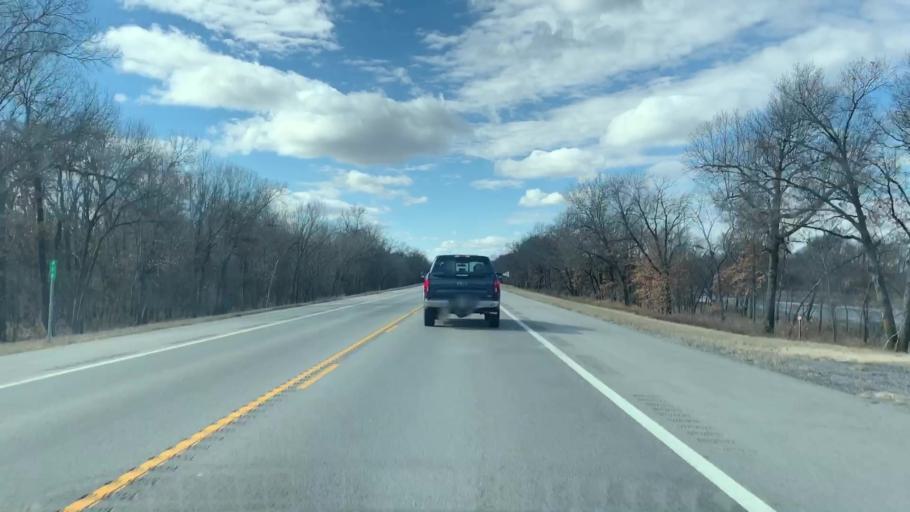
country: US
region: Kansas
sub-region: Cherokee County
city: Columbus
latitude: 37.3401
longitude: -94.9681
